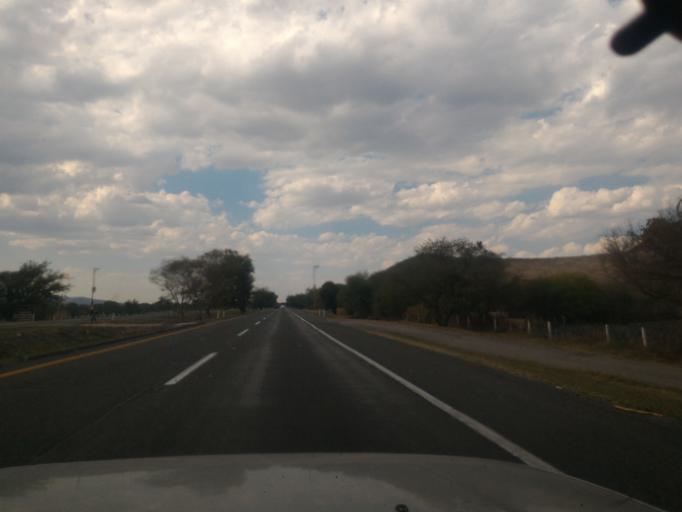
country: MX
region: Jalisco
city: Zacoalco de Torres
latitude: 20.1850
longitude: -103.5150
